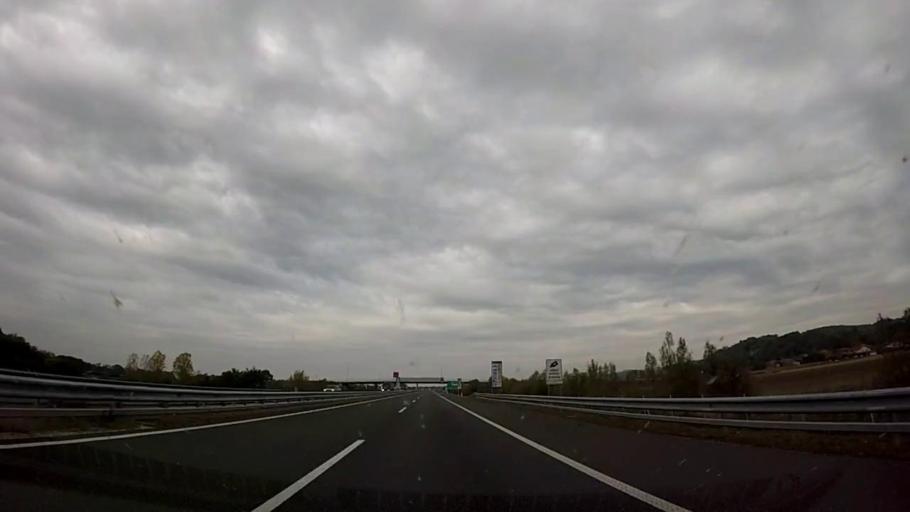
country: HR
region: Medimurska
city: Peklenica
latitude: 46.5201
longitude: 16.5243
